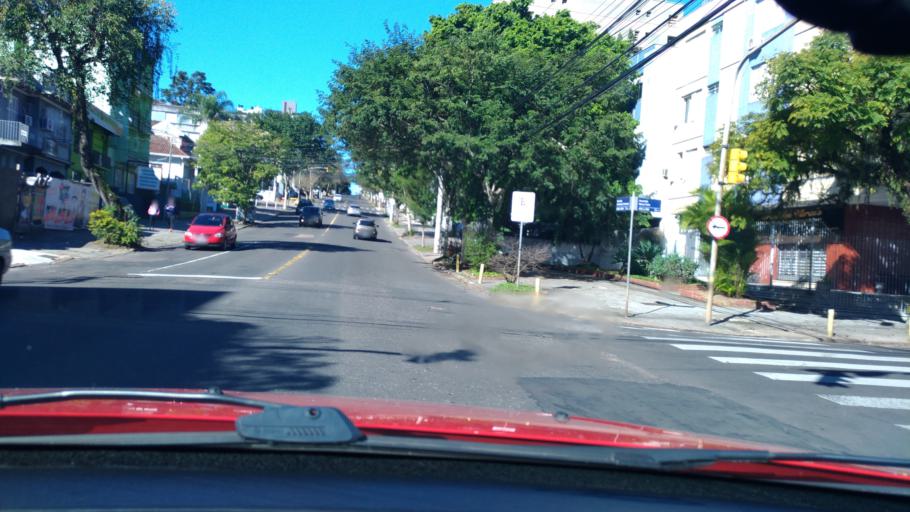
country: BR
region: Rio Grande do Sul
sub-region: Porto Alegre
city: Porto Alegre
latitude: -30.0178
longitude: -51.1955
